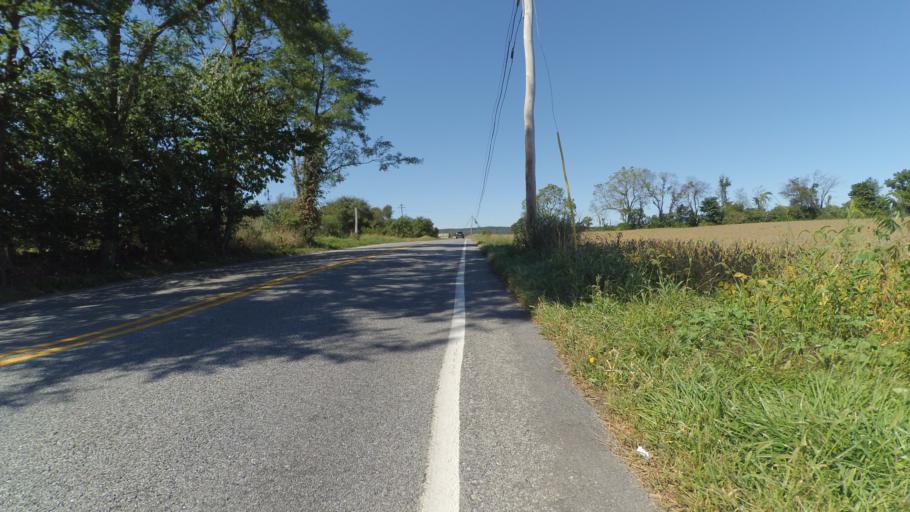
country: US
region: Pennsylvania
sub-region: Centre County
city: Pine Grove Mills
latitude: 40.7587
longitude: -77.9067
